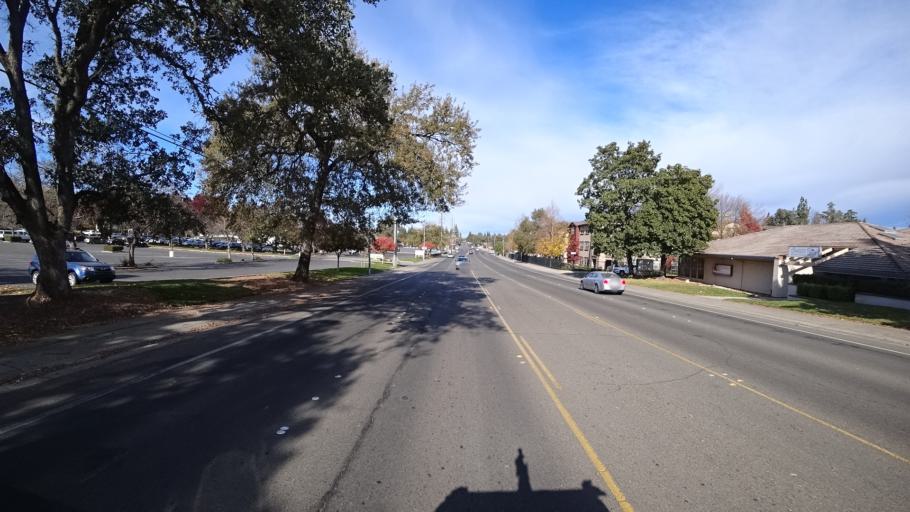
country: US
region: California
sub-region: Sacramento County
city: Fair Oaks
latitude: 38.6761
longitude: -121.2622
